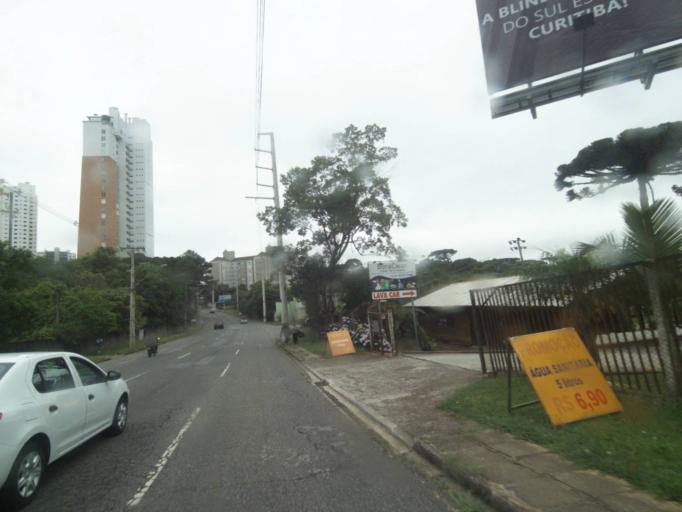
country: BR
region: Parana
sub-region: Curitiba
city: Curitiba
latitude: -25.4383
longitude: -49.3268
